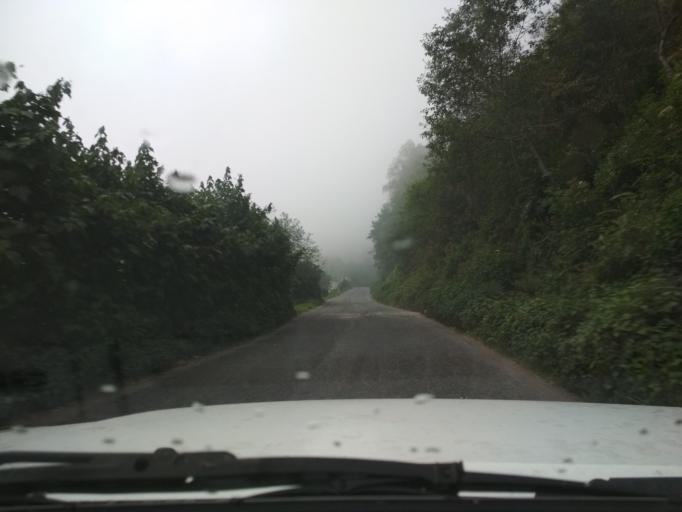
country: MX
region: Veracruz
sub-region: La Perla
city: Metlac Hernandez (Metlac Primero)
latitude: 18.9525
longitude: -97.1722
